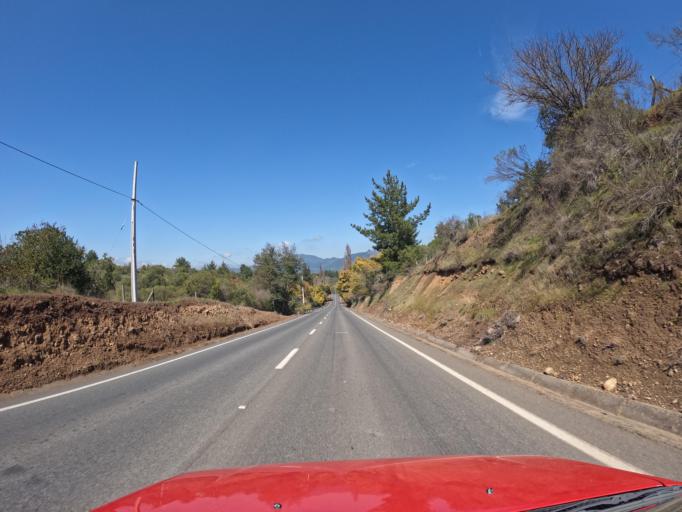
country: CL
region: Maule
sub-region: Provincia de Talca
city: San Clemente
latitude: -35.4522
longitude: -71.2700
